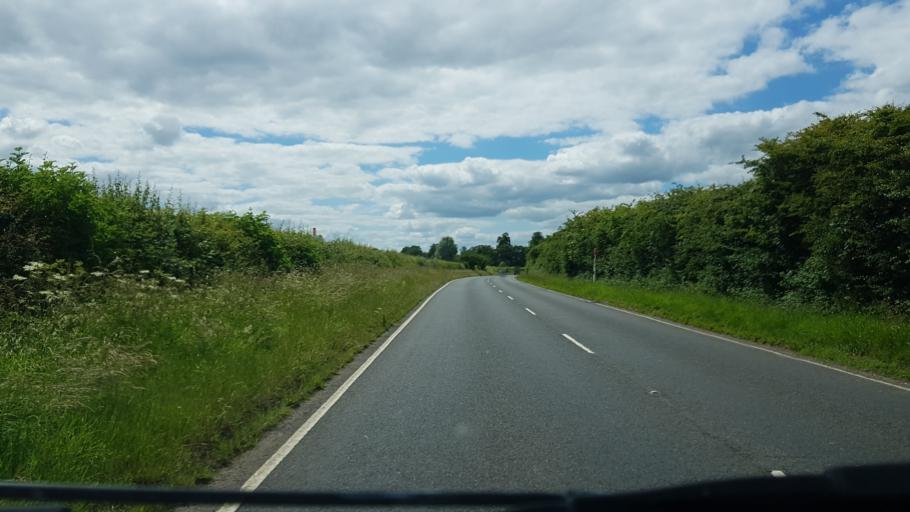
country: GB
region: England
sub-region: Worcestershire
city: Bromsgrove
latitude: 52.2607
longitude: -2.0656
